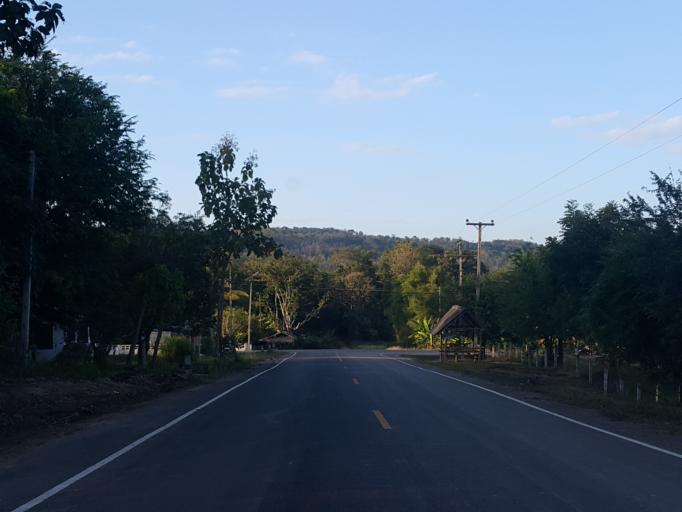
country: TH
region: Lampang
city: Lampang
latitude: 18.4373
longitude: 99.5700
